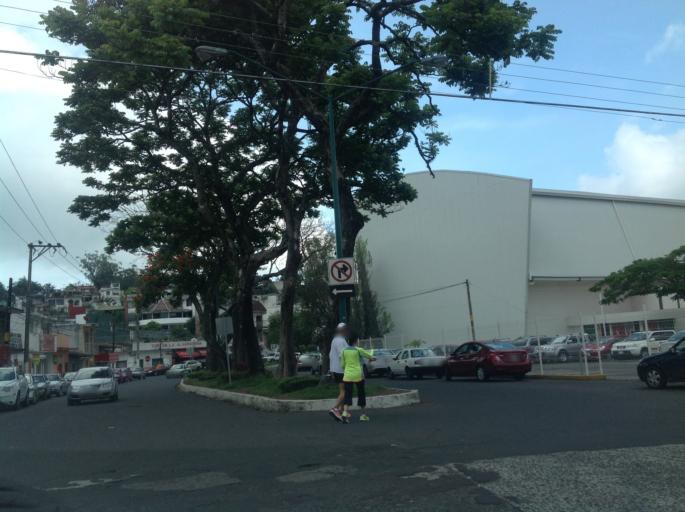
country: MX
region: Veracruz
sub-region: Xalapa
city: Xalapa de Enriquez
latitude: 19.5238
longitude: -96.9207
